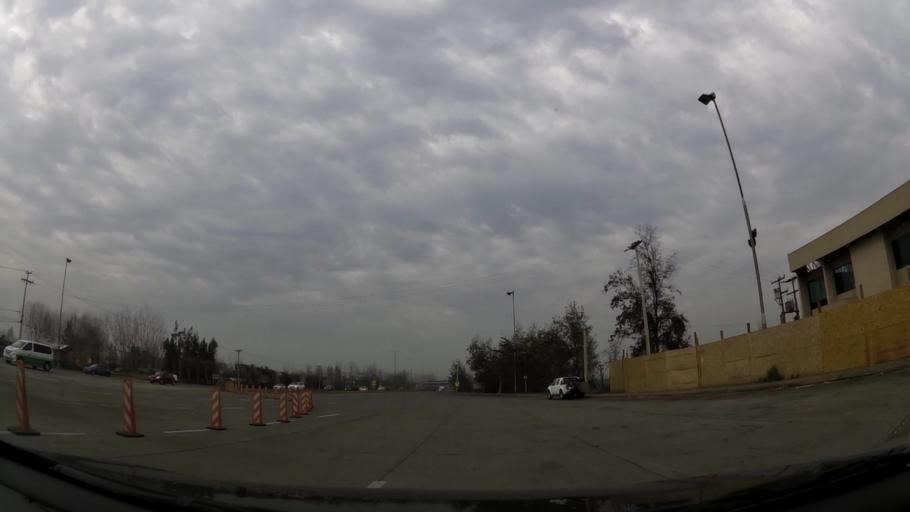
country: CL
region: Santiago Metropolitan
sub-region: Provincia de Chacabuco
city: Chicureo Abajo
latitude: -33.2367
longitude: -70.7587
